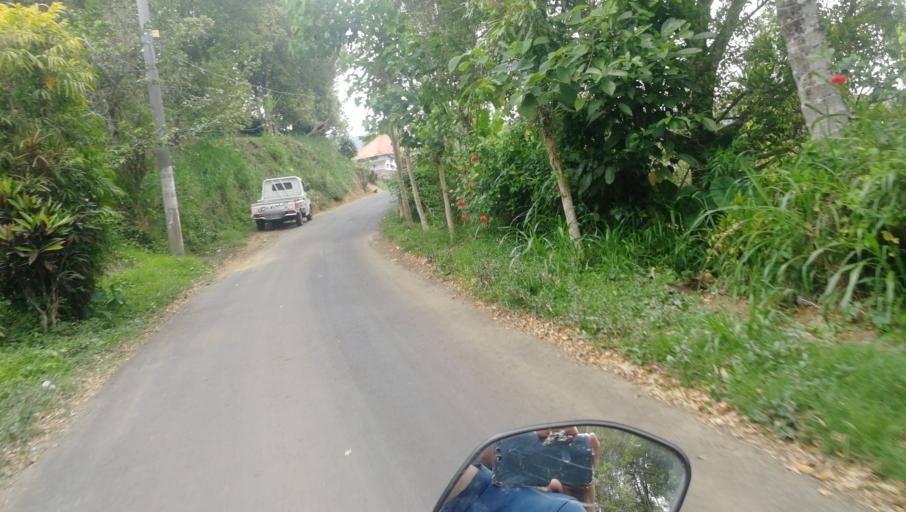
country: ID
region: Bali
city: Munduk
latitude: -8.2846
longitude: 115.0366
